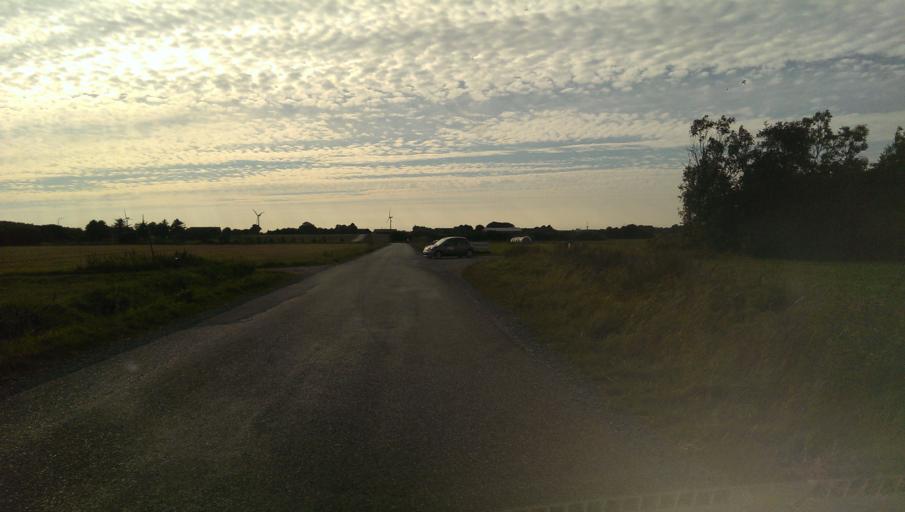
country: DK
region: South Denmark
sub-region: Esbjerg Kommune
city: Tjaereborg
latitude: 55.4782
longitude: 8.5666
